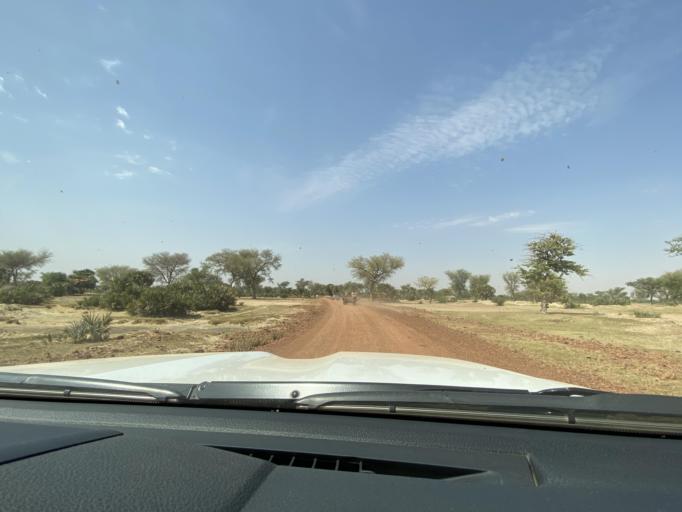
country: NE
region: Dosso
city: Birnin Gaoure
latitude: 13.2470
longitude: 2.8572
